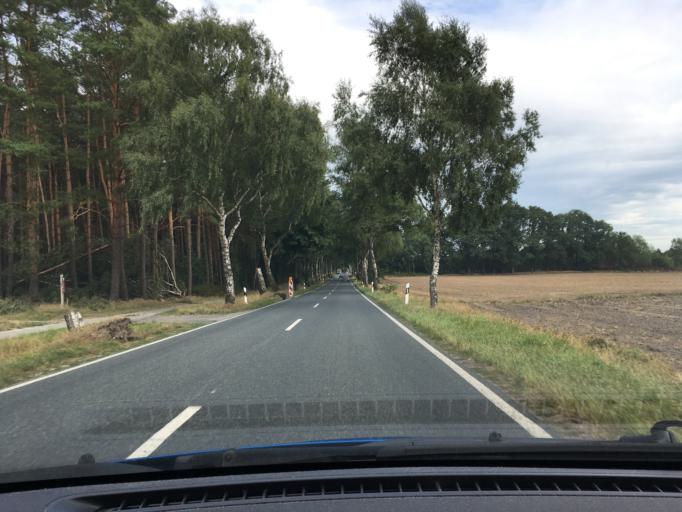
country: DE
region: Lower Saxony
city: Undeloh
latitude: 53.1982
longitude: 9.9968
